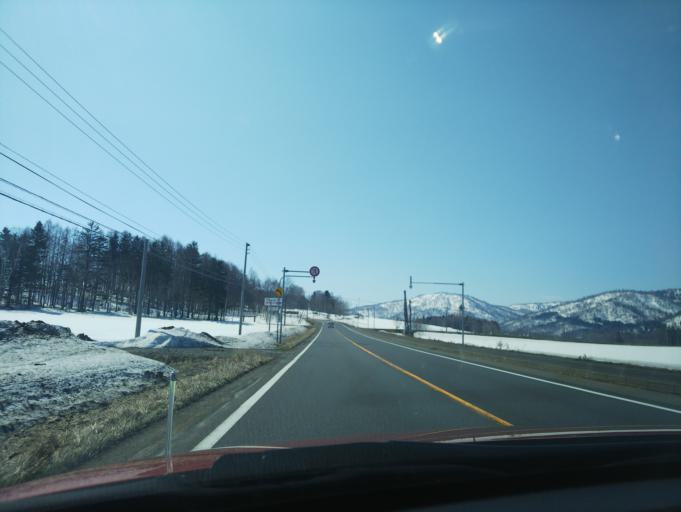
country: JP
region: Hokkaido
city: Nayoro
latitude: 44.6679
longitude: 142.2685
